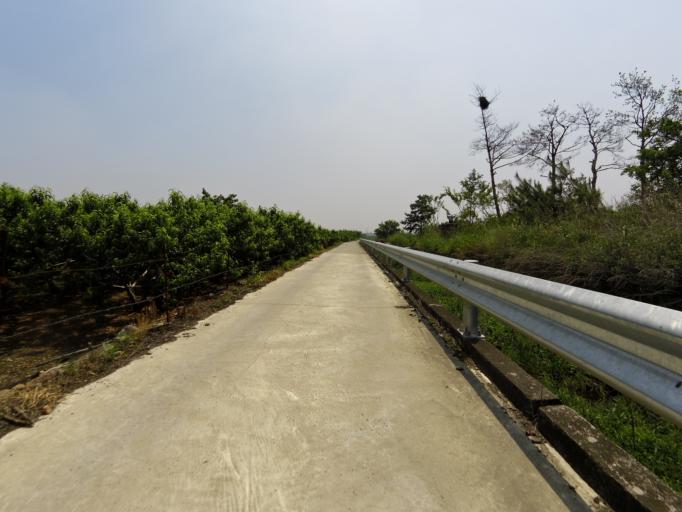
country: KR
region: Gyeongsangbuk-do
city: Gyeongsan-si
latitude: 35.8500
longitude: 128.7295
